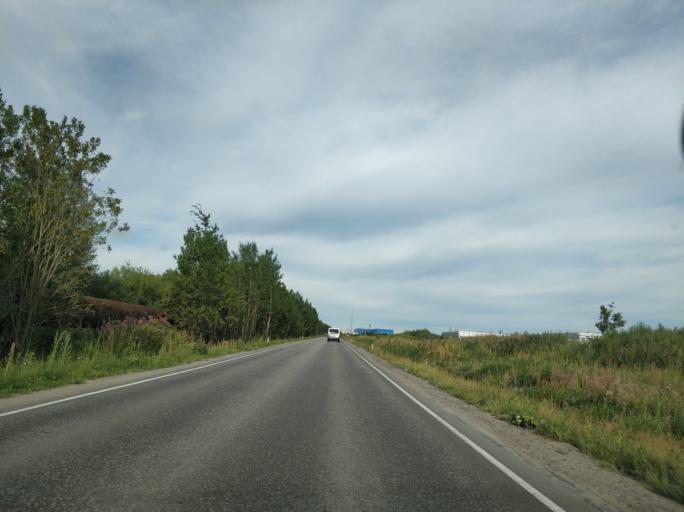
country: RU
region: St.-Petersburg
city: Grazhdanka
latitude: 60.0456
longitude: 30.4217
